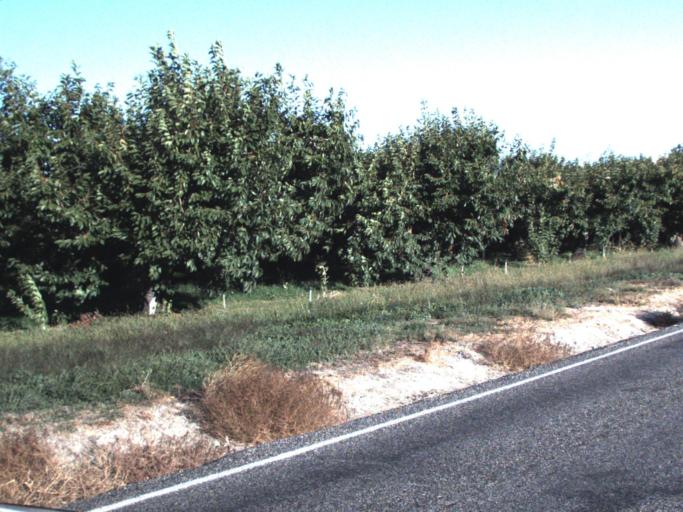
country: US
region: Washington
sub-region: Benton County
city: Benton City
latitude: 46.2870
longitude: -119.4940
